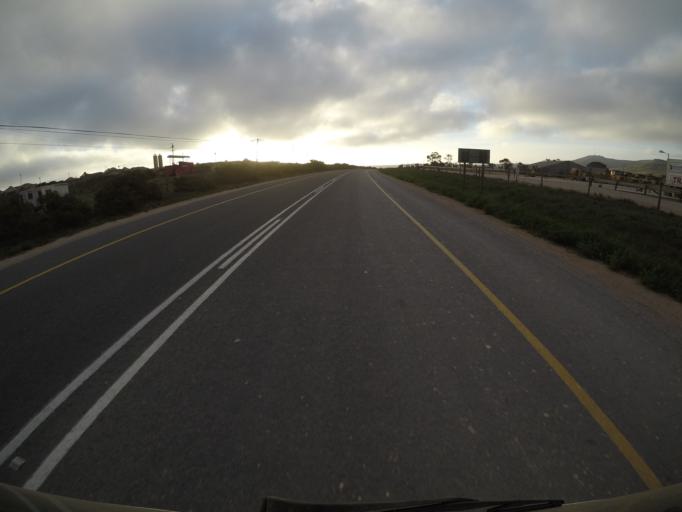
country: ZA
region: Western Cape
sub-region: Eden District Municipality
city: Mossel Bay
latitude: -34.1129
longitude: 22.0792
